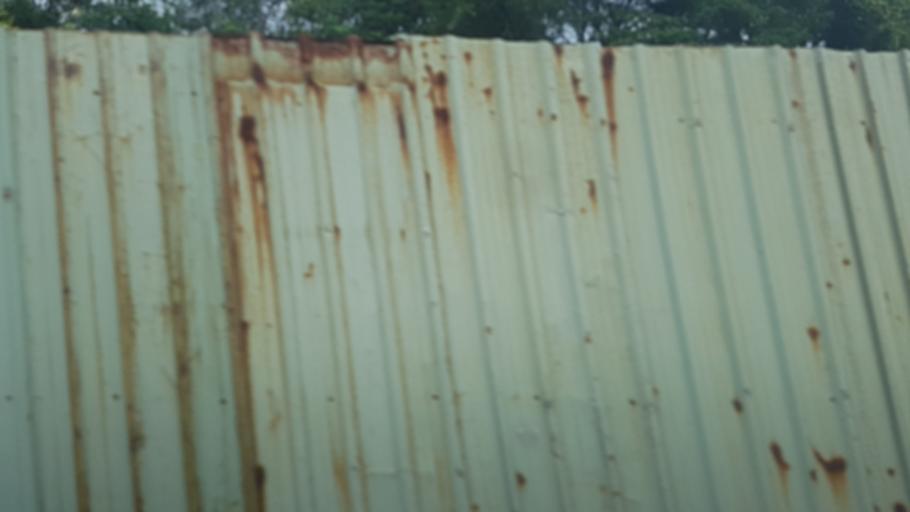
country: TW
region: Taiwan
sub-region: Hsinchu
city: Hsinchu
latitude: 24.7802
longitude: 120.9347
